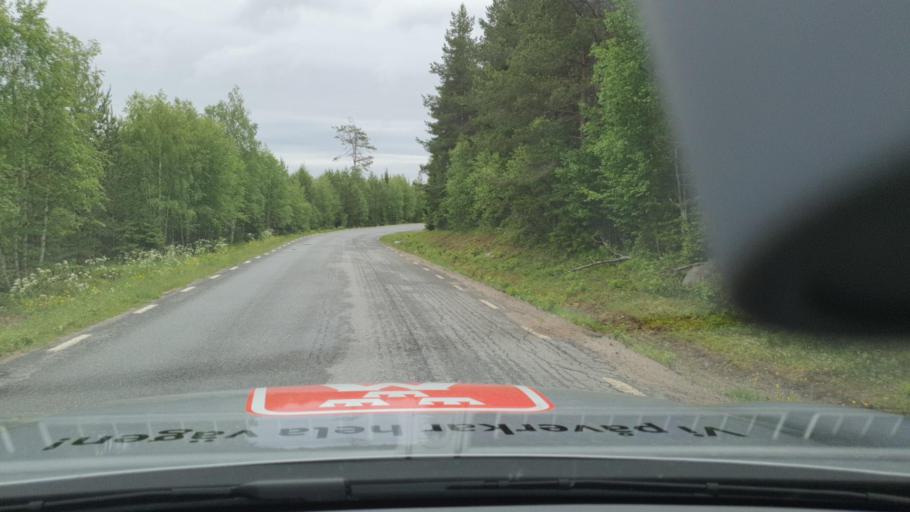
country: SE
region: Norrbotten
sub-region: Lulea Kommun
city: Ranea
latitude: 65.7921
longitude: 22.3066
